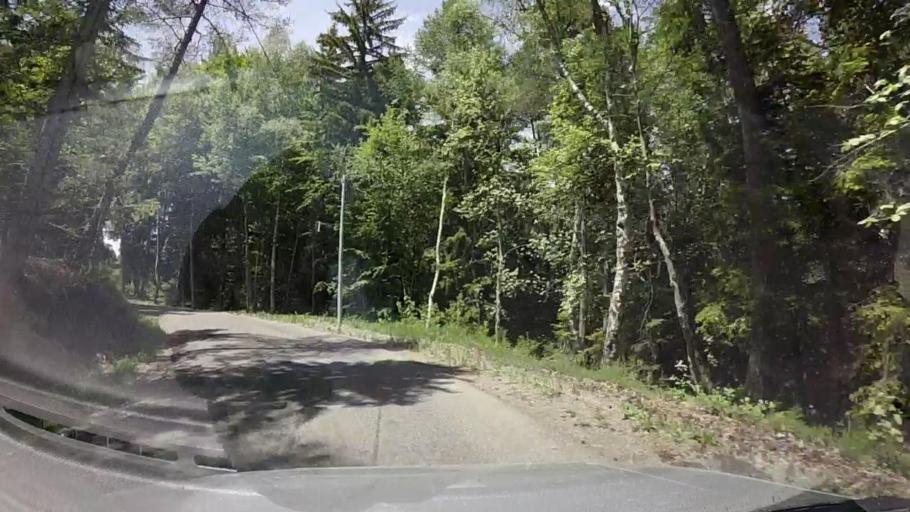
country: FR
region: Provence-Alpes-Cote d'Azur
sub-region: Departement des Alpes-de-Haute-Provence
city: Seyne-les-Alpes
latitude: 44.3323
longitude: 6.3344
